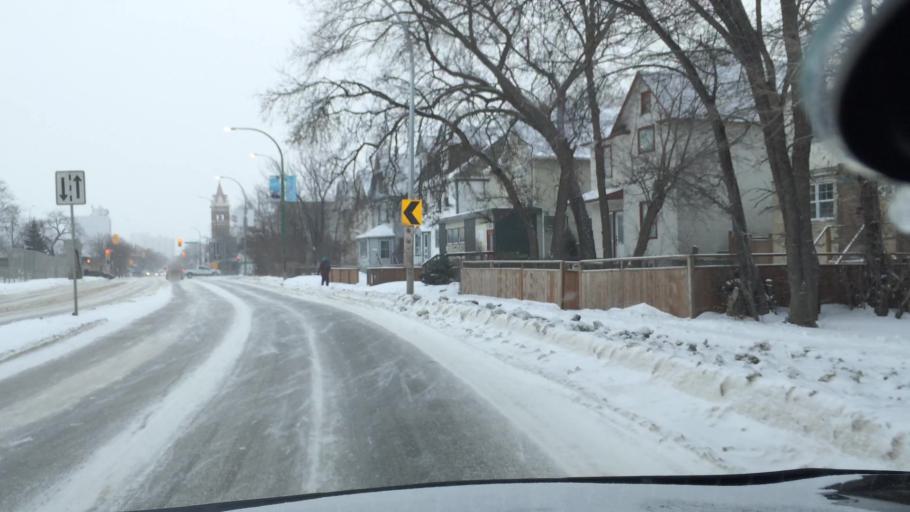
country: CA
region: Manitoba
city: Winnipeg
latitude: 49.8859
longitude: -97.1627
